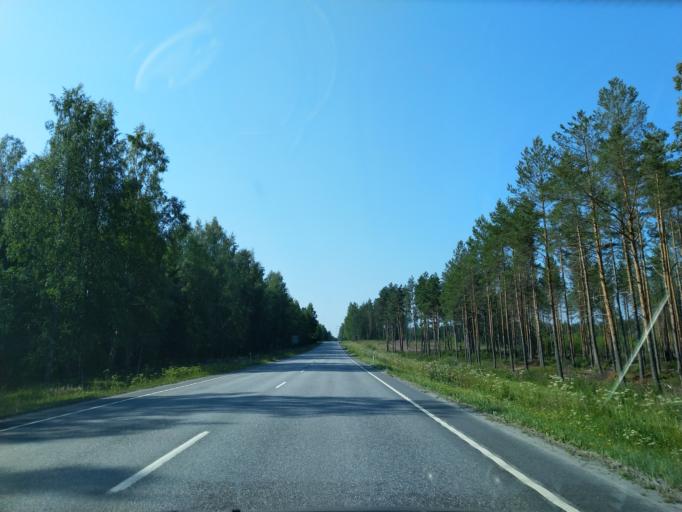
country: FI
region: Satakunta
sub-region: Pori
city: Pomarkku
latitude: 61.6669
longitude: 21.9752
